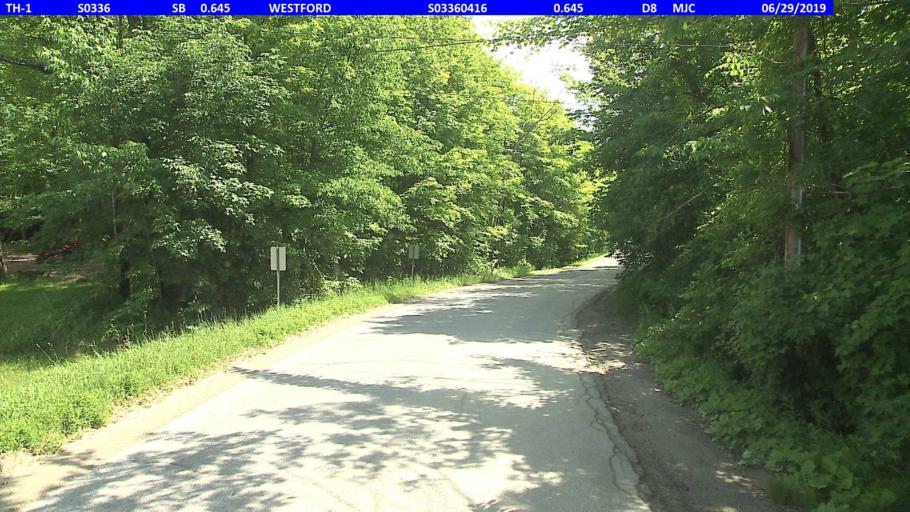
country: US
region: Vermont
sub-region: Chittenden County
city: Milton
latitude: 44.5734
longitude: -73.0579
